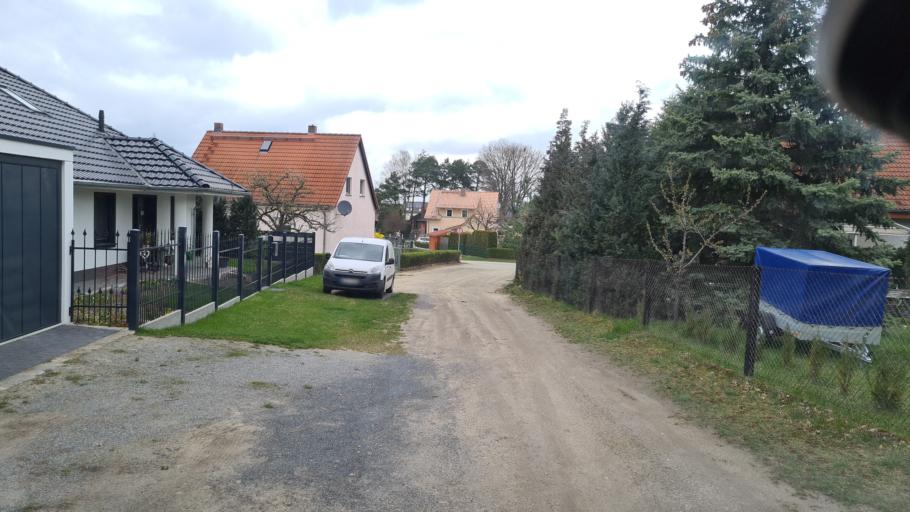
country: DE
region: Brandenburg
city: Senftenberg
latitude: 51.4925
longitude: 14.0607
